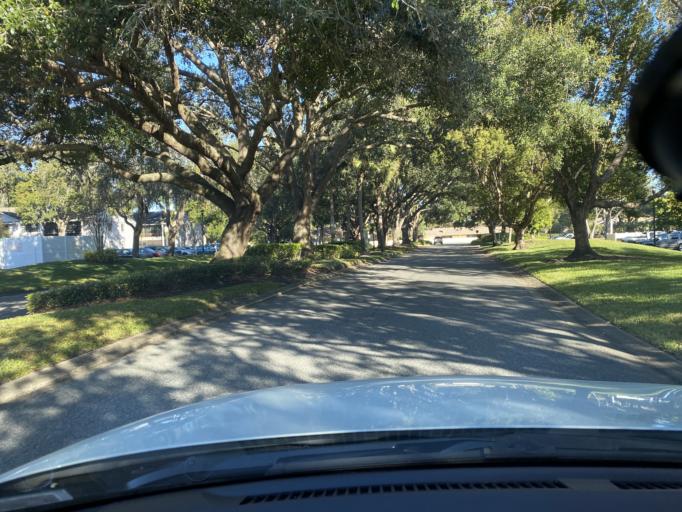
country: US
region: Florida
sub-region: Orange County
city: Azalea Park
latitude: 28.5160
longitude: -81.3053
